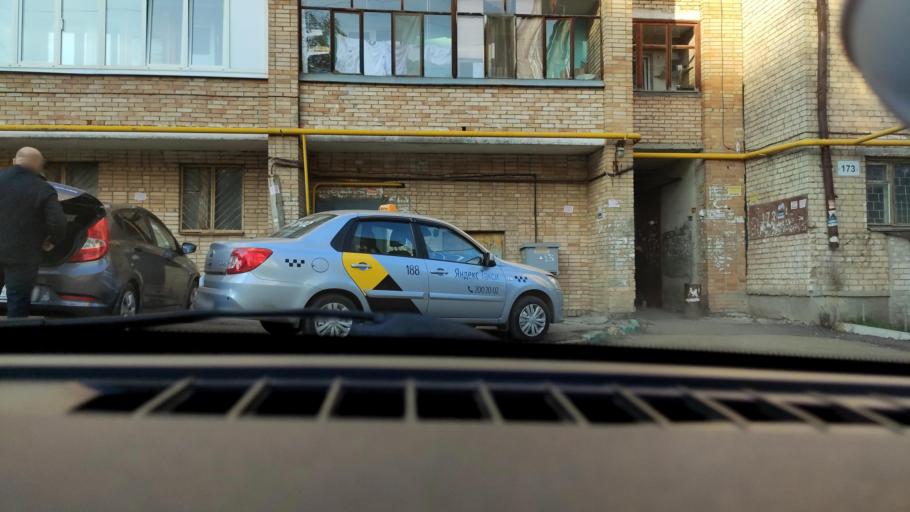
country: RU
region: Samara
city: Samara
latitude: 53.1869
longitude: 50.1976
